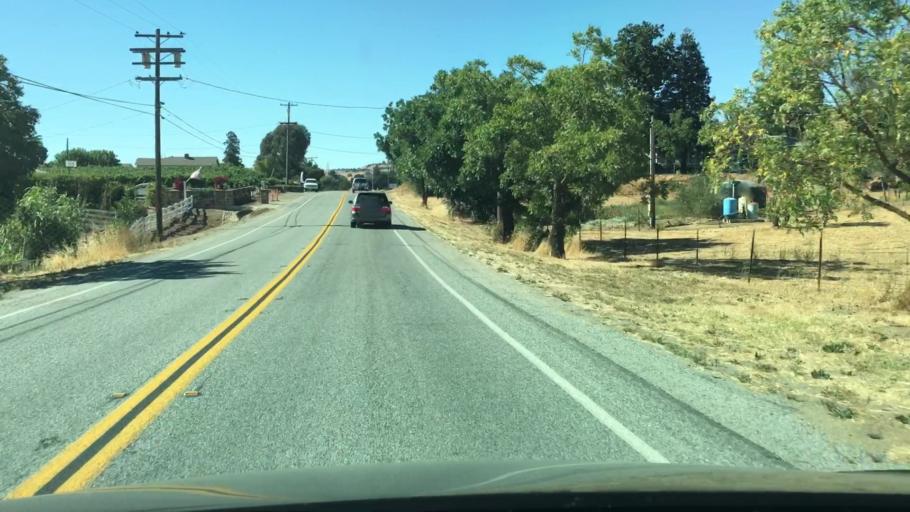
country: US
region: California
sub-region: Santa Clara County
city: San Martin
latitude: 37.0831
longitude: -121.5647
